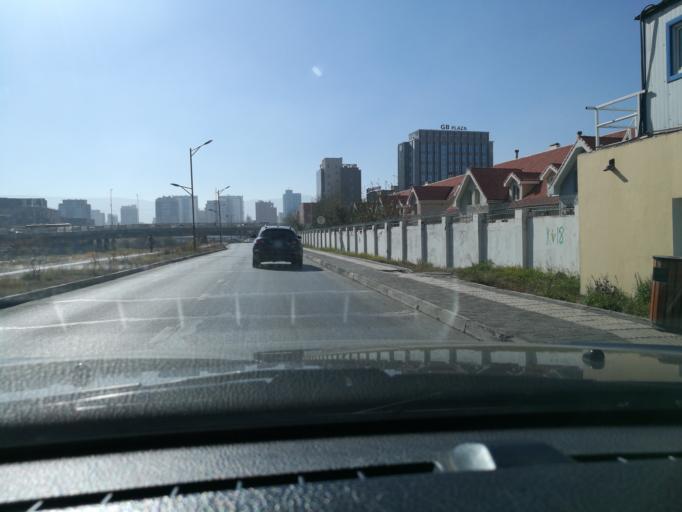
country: MN
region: Ulaanbaatar
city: Ulaanbaatar
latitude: 47.9247
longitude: 106.9313
